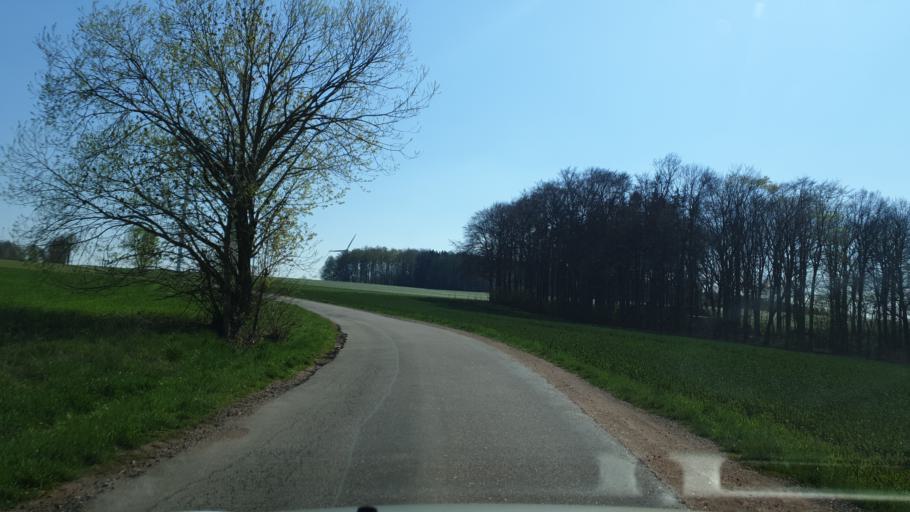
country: DE
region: Saxony
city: Bernsdorf
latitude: 50.7707
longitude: 12.6832
